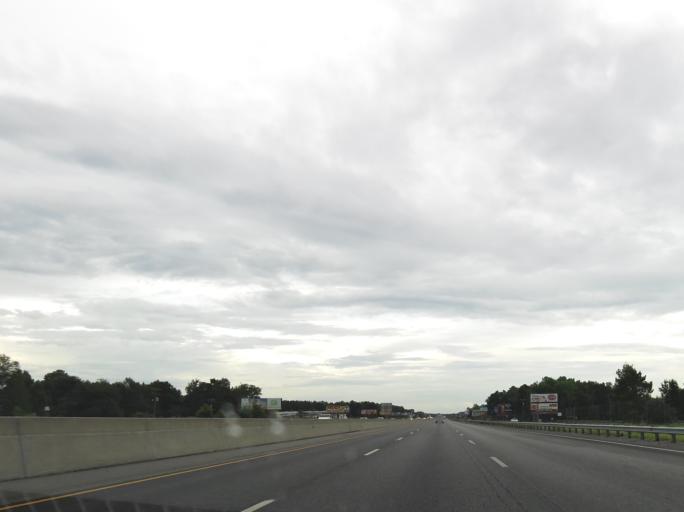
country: US
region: Georgia
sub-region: Lowndes County
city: Remerton
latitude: 30.8886
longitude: -83.3518
